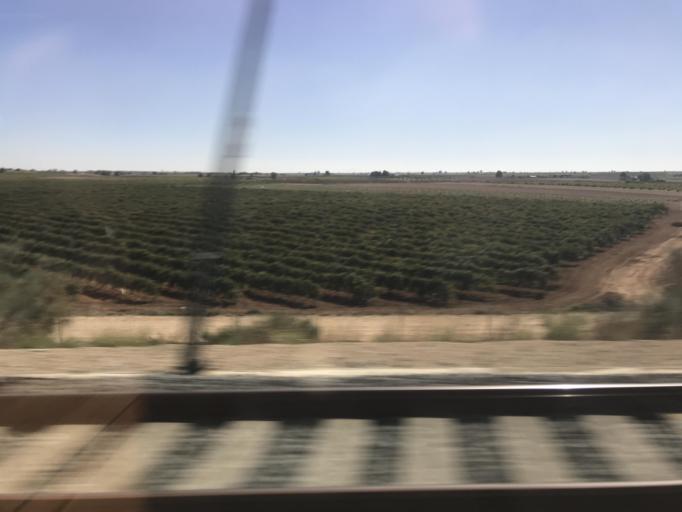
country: ES
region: Castille-La Mancha
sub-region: Province of Toledo
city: Santa Cruz de la Zarza
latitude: 39.9779
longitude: -3.1498
